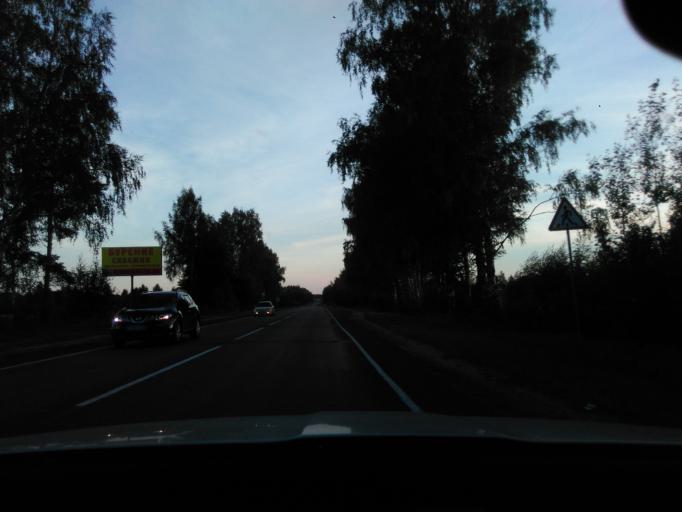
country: RU
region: Tverskaya
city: Zavidovo
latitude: 56.6031
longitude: 36.6241
